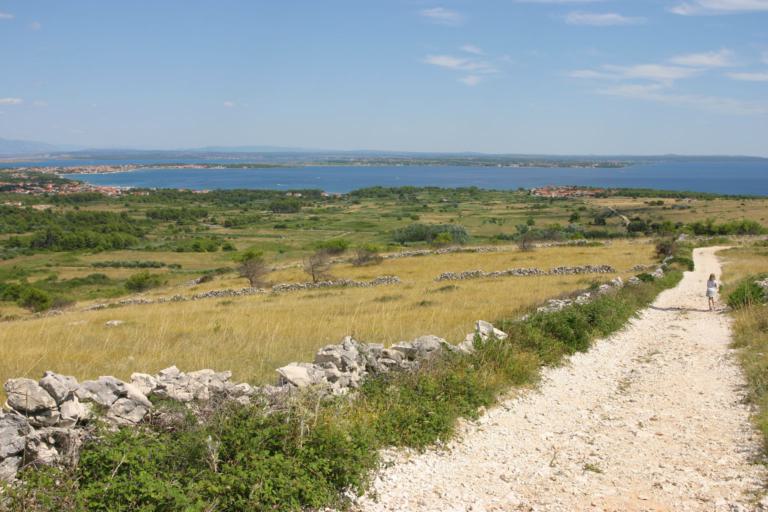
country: HR
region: Zadarska
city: Vir
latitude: 44.3019
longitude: 15.0529
